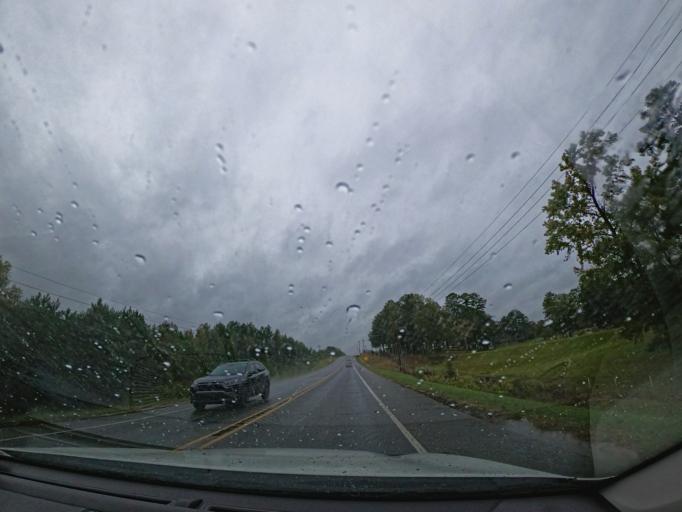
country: US
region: Louisiana
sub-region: Webster Parish
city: Minden
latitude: 32.6075
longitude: -93.2498
